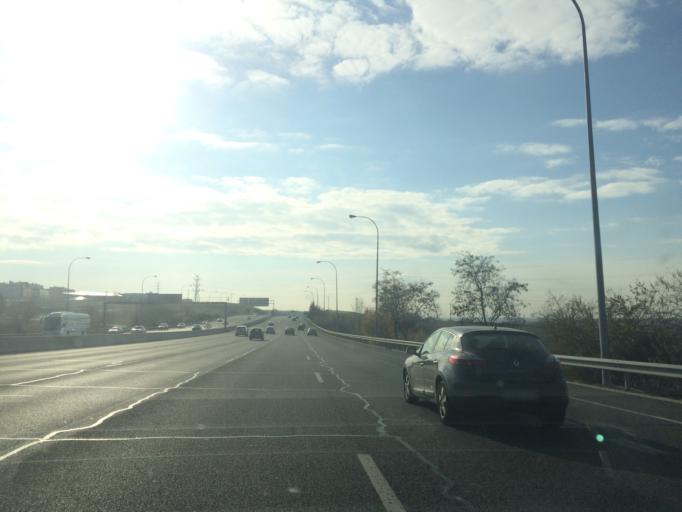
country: ES
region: Madrid
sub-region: Provincia de Madrid
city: Las Tablas
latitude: 40.5169
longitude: -3.6929
